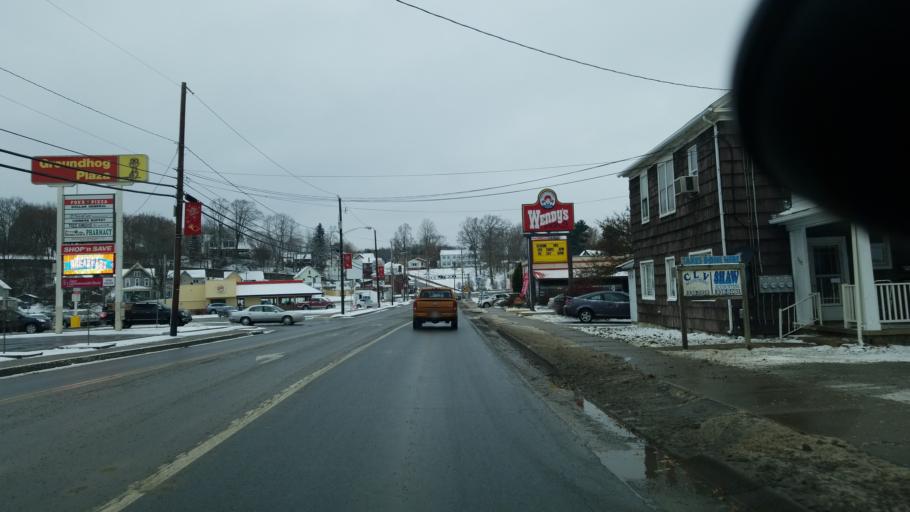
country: US
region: Pennsylvania
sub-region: Jefferson County
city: Punxsutawney
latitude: 40.9456
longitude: -78.9676
